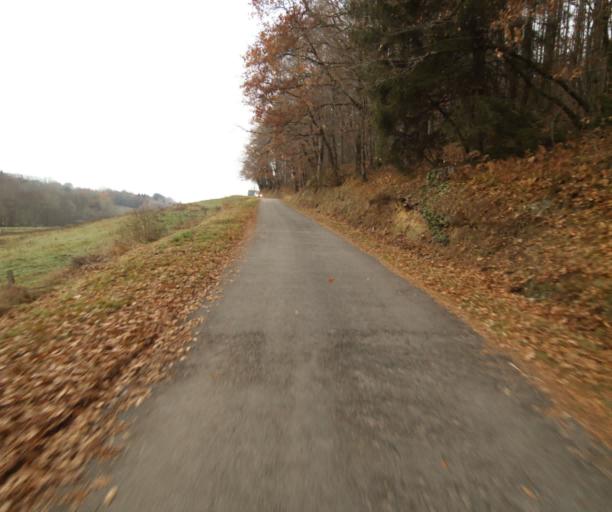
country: FR
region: Limousin
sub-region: Departement de la Correze
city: Sainte-Fortunade
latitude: 45.2257
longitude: 1.7503
